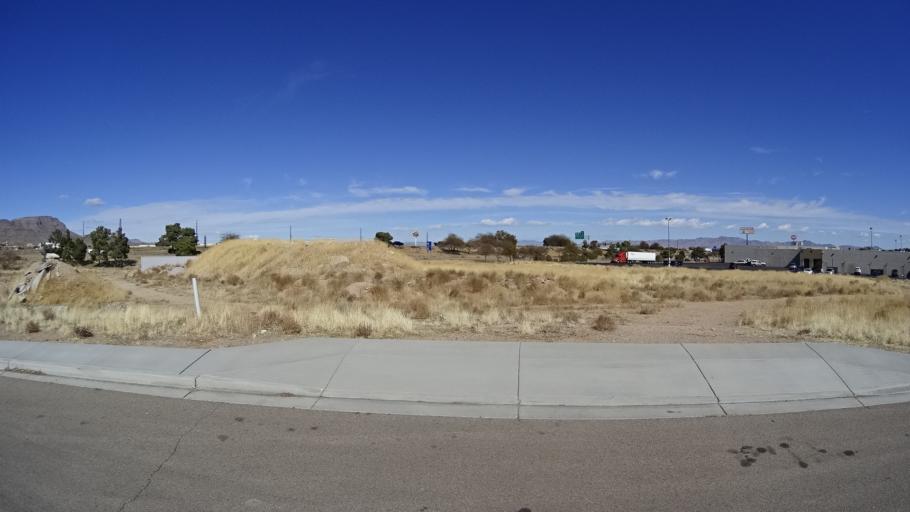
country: US
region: Arizona
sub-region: Mohave County
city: Kingman
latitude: 35.2153
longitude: -114.0382
